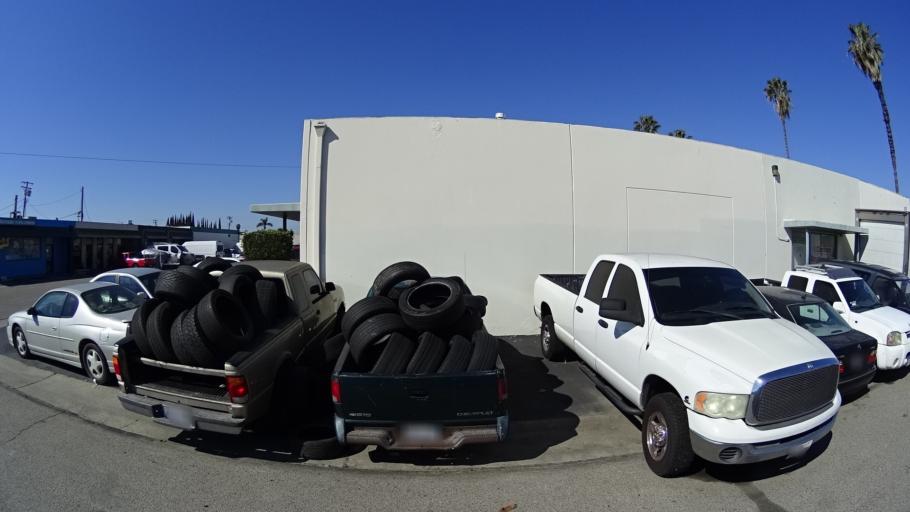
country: US
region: California
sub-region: Orange County
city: Anaheim
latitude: 33.8274
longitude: -117.9312
